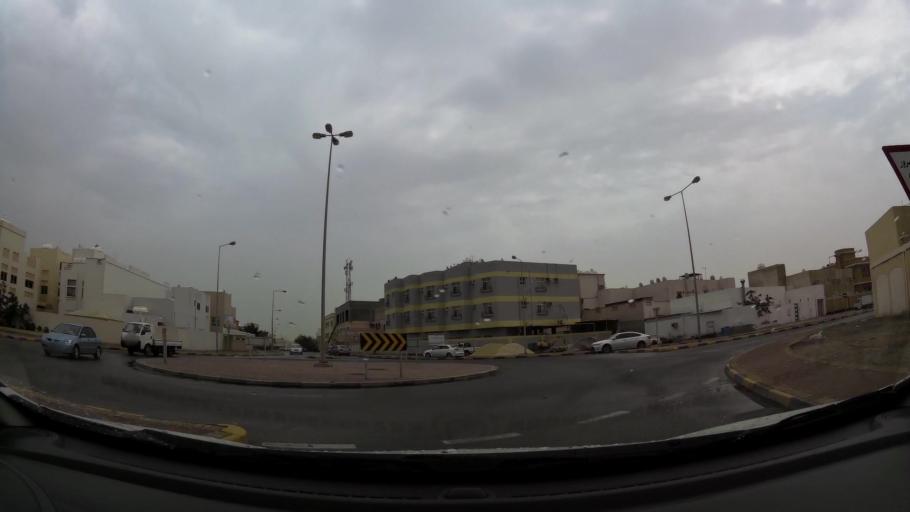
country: BH
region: Northern
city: Madinat `Isa
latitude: 26.1565
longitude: 50.5779
